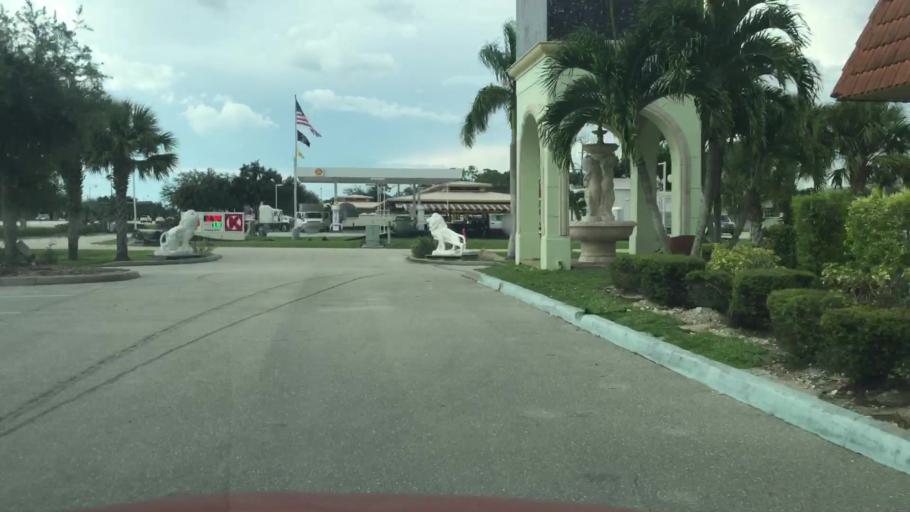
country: US
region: Florida
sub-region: Lee County
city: Bonita Springs
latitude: 26.3774
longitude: -81.8073
